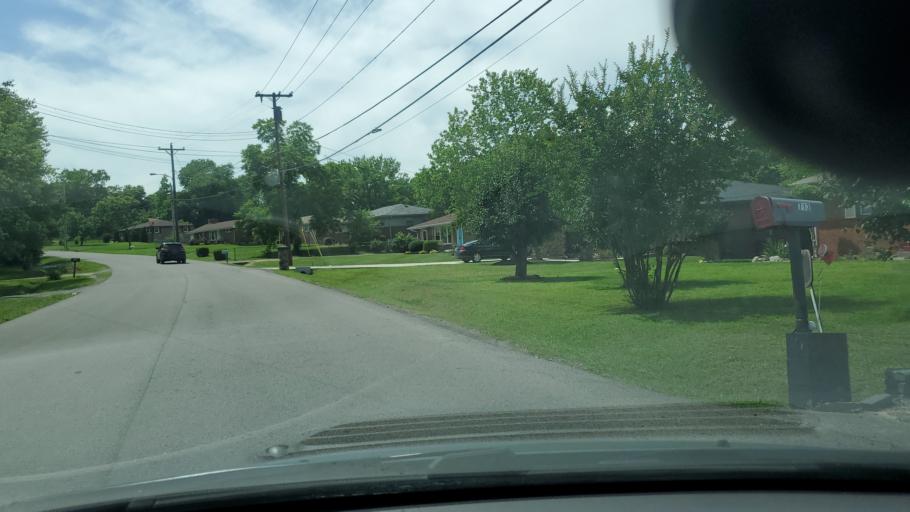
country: US
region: Tennessee
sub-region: Davidson County
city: Nashville
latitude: 36.2368
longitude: -86.7376
